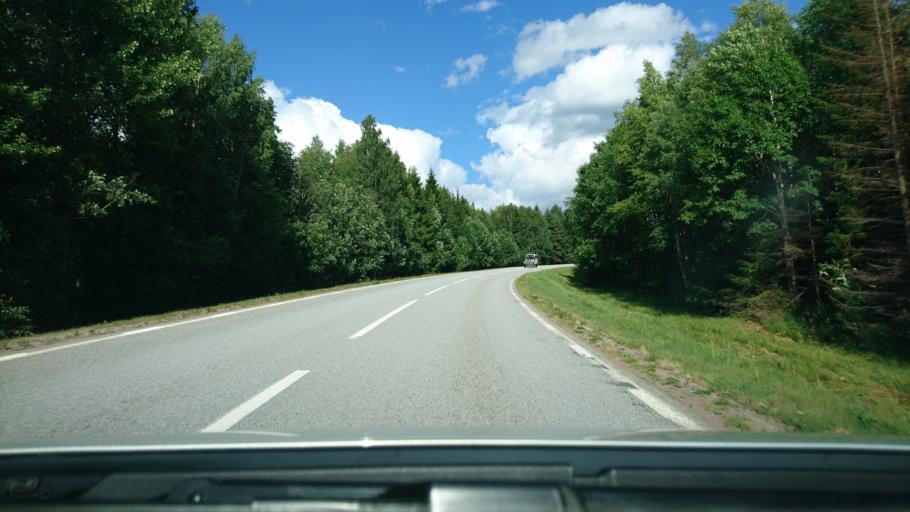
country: SE
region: Vaesternorrland
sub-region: Solleftea Kommun
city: As
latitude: 63.7172
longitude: 16.9515
